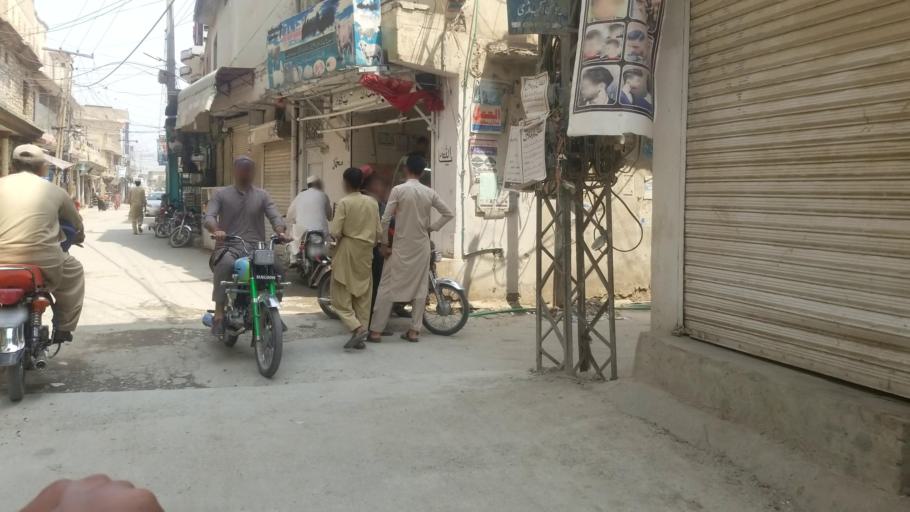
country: PK
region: Khyber Pakhtunkhwa
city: Peshawar
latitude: 34.0306
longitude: 71.5855
